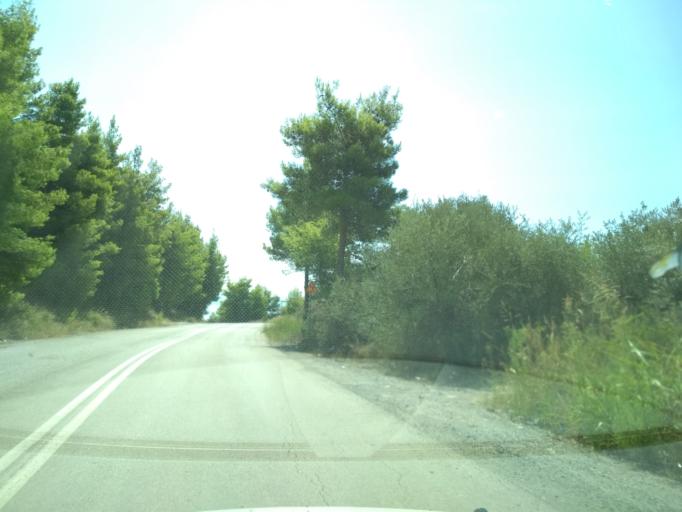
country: GR
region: Central Greece
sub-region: Nomos Evvoias
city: Roviai
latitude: 38.8192
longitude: 23.2304
